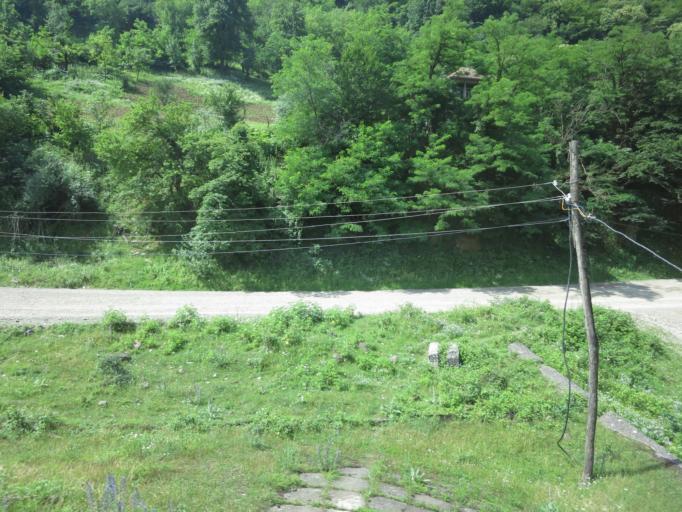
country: GE
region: Imereti
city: Kharagauli
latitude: 42.0046
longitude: 43.2216
